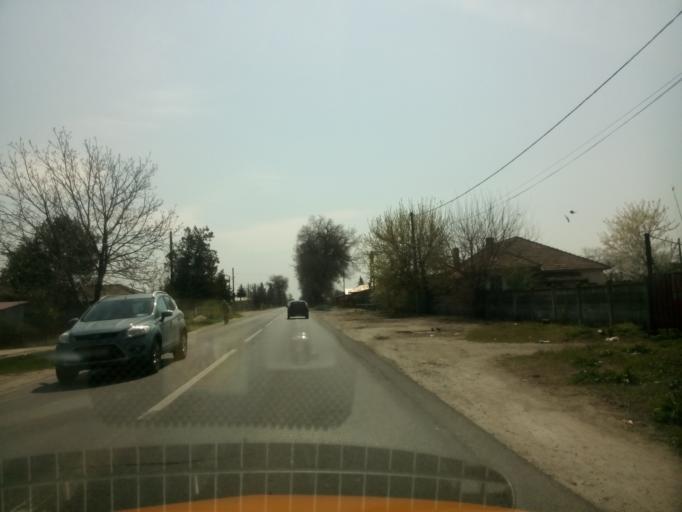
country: RO
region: Calarasi
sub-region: Comuna Frumusani
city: Frumusani
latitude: 44.2800
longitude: 26.3327
